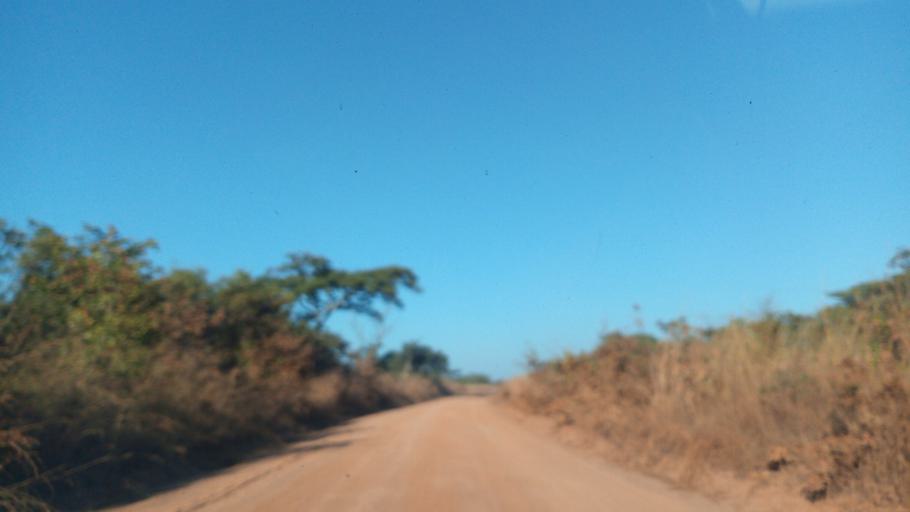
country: ZM
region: Luapula
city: Mwense
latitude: -10.5002
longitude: 28.4809
